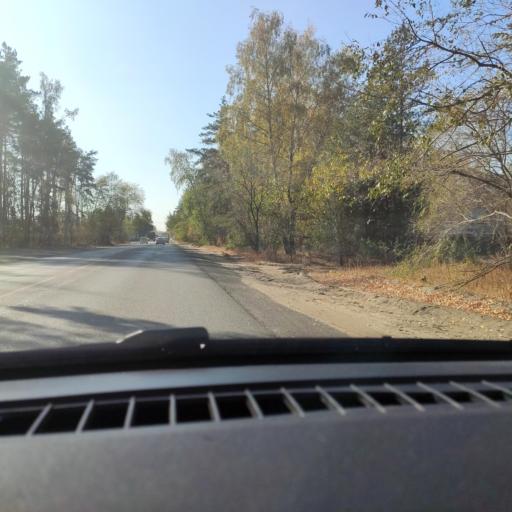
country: RU
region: Voronezj
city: Pridonskoy
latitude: 51.6831
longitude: 39.0970
